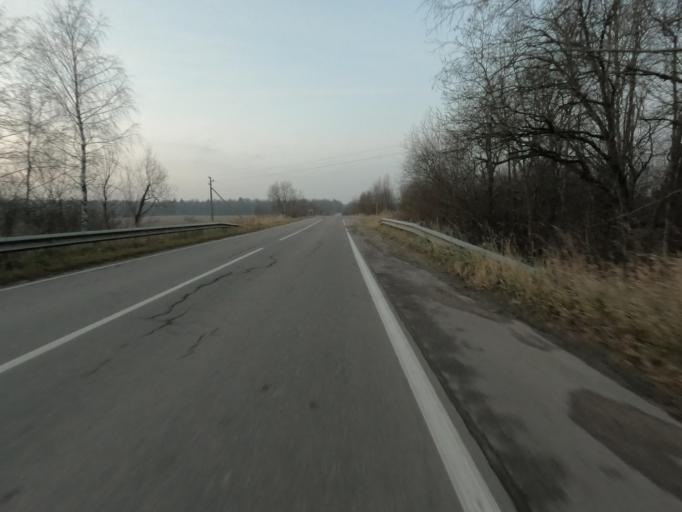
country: RU
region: Leningrad
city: Kirovsk
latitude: 59.8617
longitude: 30.9814
